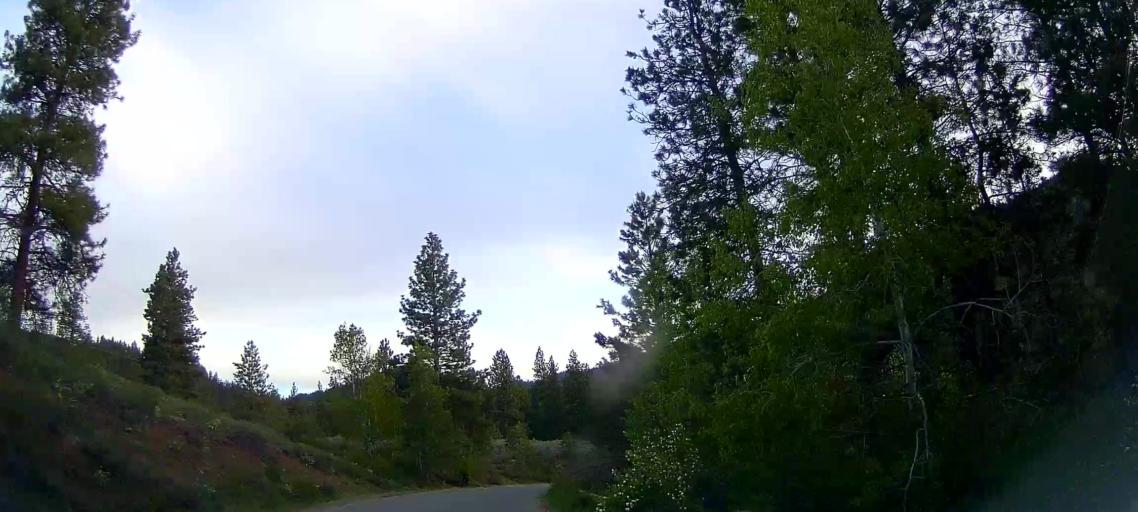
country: US
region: Washington
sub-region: Chelan County
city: Granite Falls
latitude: 48.4664
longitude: -120.2592
